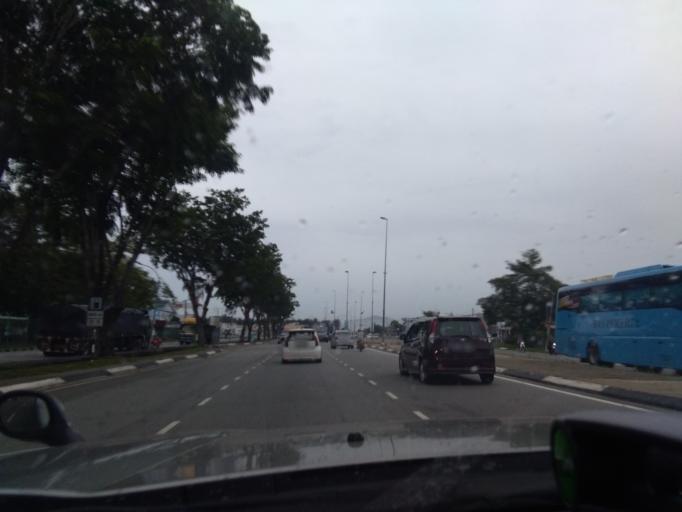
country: MY
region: Penang
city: Nibong Tebal
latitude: 5.1764
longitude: 100.4816
